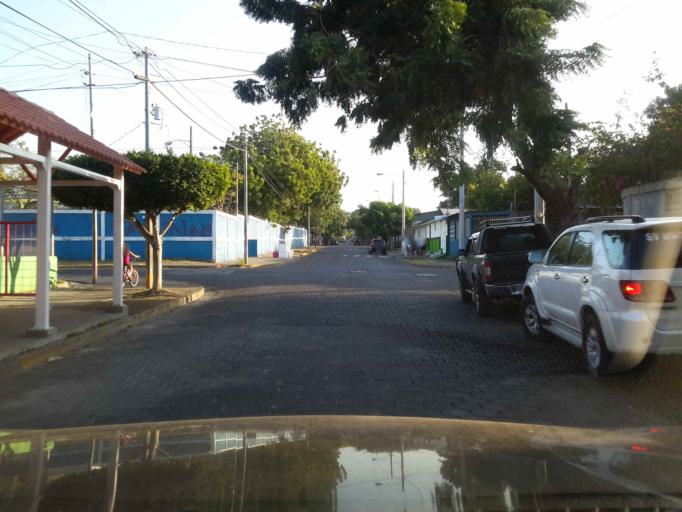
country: NI
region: Managua
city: Ciudad Sandino
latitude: 12.1557
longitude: -86.2998
